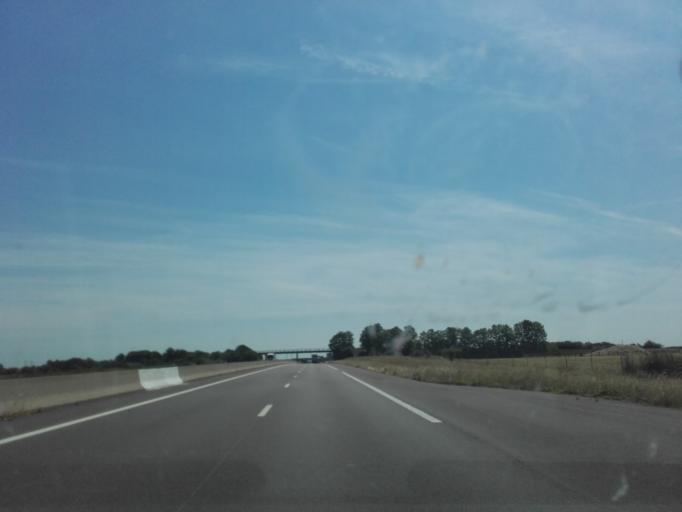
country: FR
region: Bourgogne
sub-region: Departement de la Cote-d'Or
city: Semur-en-Auxois
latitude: 47.4885
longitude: 4.1443
